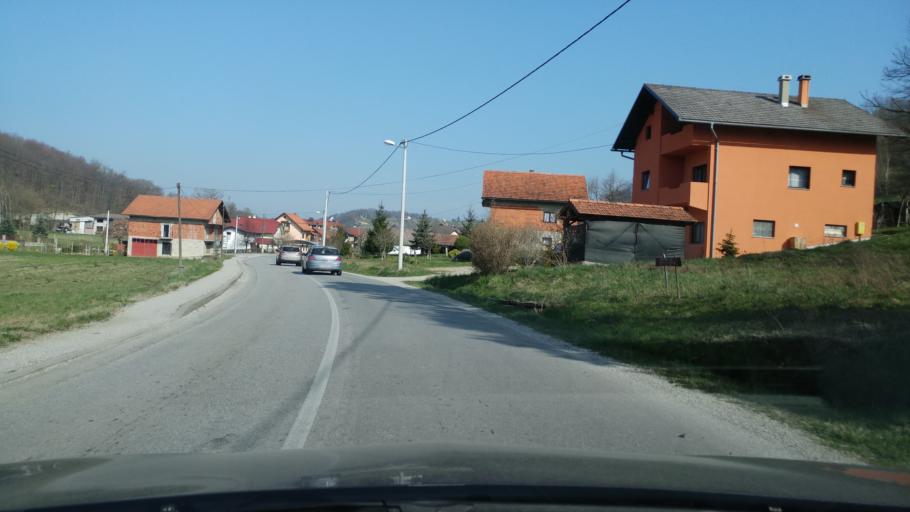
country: HR
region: Zagrebacka
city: Pojatno
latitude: 45.9049
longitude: 15.7817
